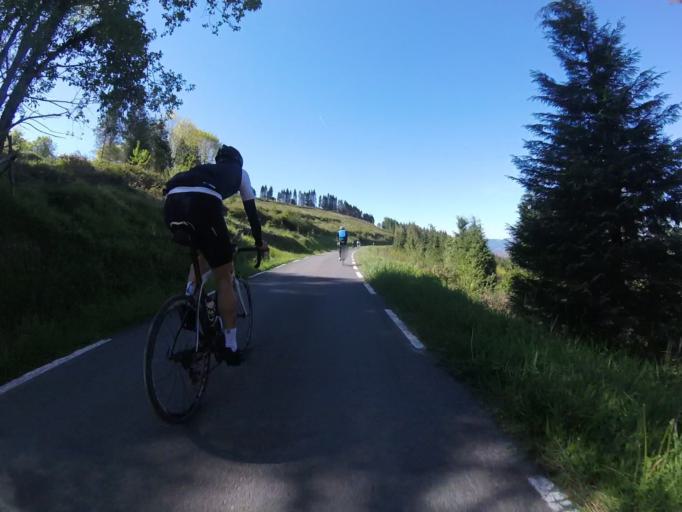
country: ES
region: Basque Country
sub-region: Provincia de Guipuzcoa
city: Errezil
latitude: 43.1939
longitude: -2.2012
